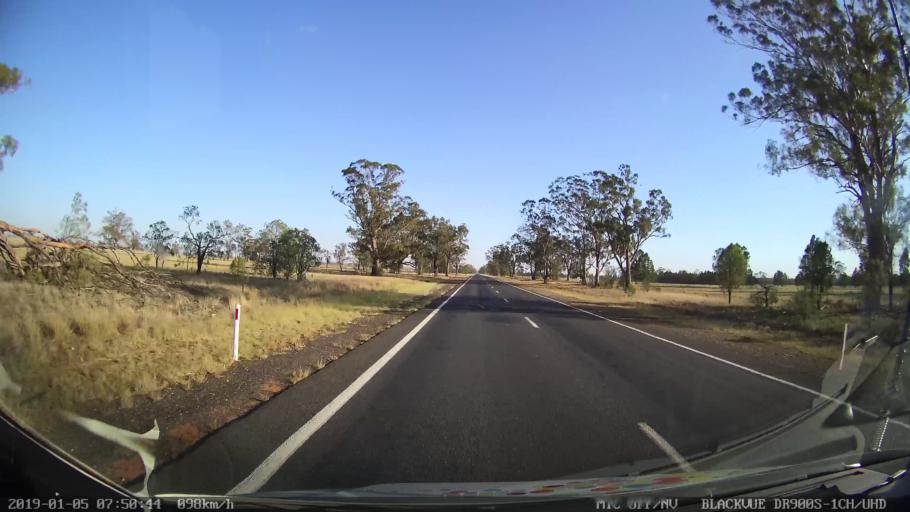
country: AU
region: New South Wales
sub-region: Gilgandra
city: Gilgandra
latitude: -31.7833
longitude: 148.6380
